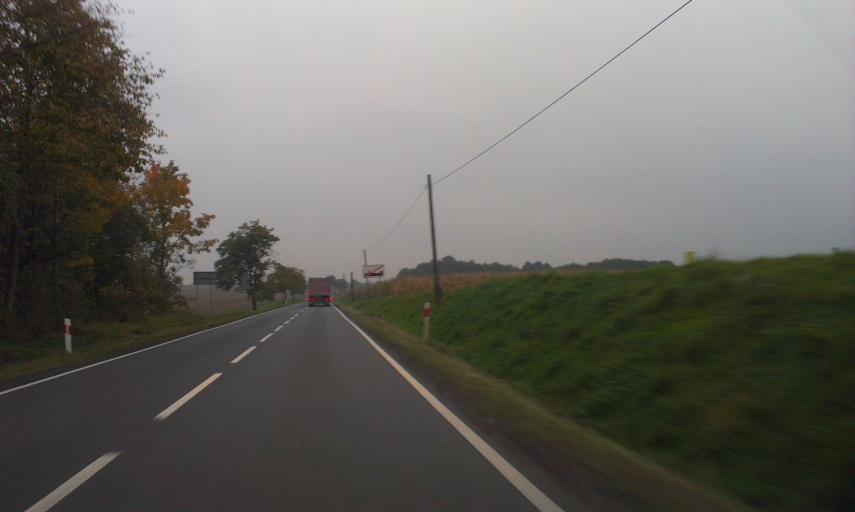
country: PL
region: Kujawsko-Pomorskie
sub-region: Powiat sepolenski
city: Sepolno Krajenskie
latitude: 53.4379
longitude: 17.6074
